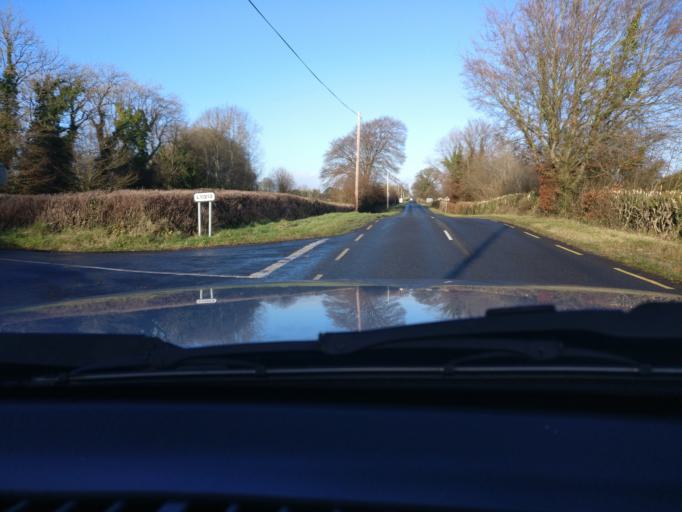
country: IE
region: Leinster
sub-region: An Iarmhi
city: An Muileann gCearr
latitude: 53.4777
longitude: -7.4493
